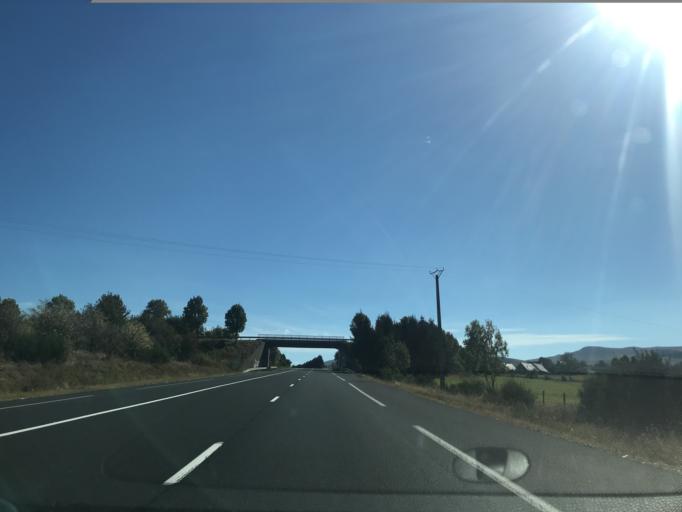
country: FR
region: Auvergne
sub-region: Departement du Puy-de-Dome
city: La Bourboule
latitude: 45.6646
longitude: 2.7453
